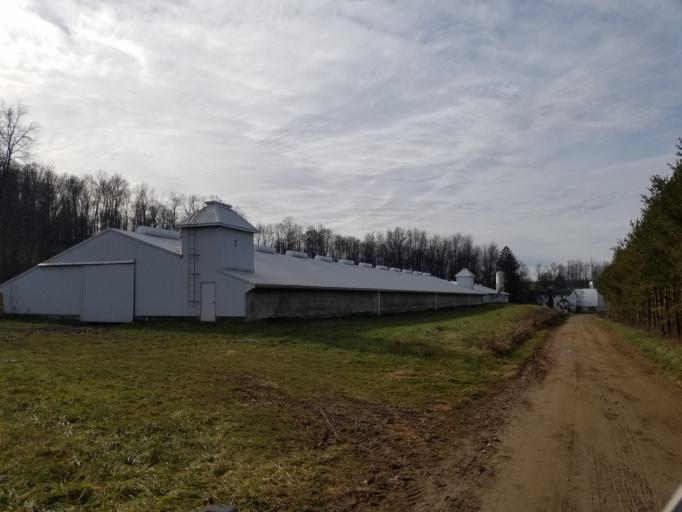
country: US
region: Ohio
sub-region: Knox County
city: Danville
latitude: 40.5482
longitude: -82.3697
